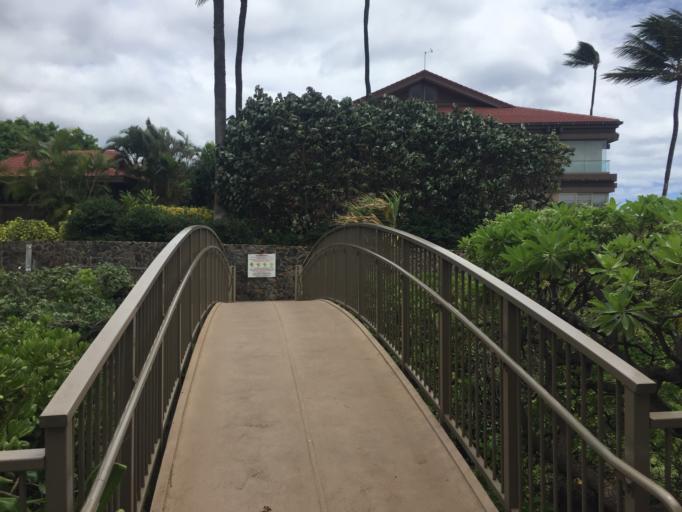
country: US
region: Hawaii
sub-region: Maui County
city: Kihei
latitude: 20.6807
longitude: -156.4437
